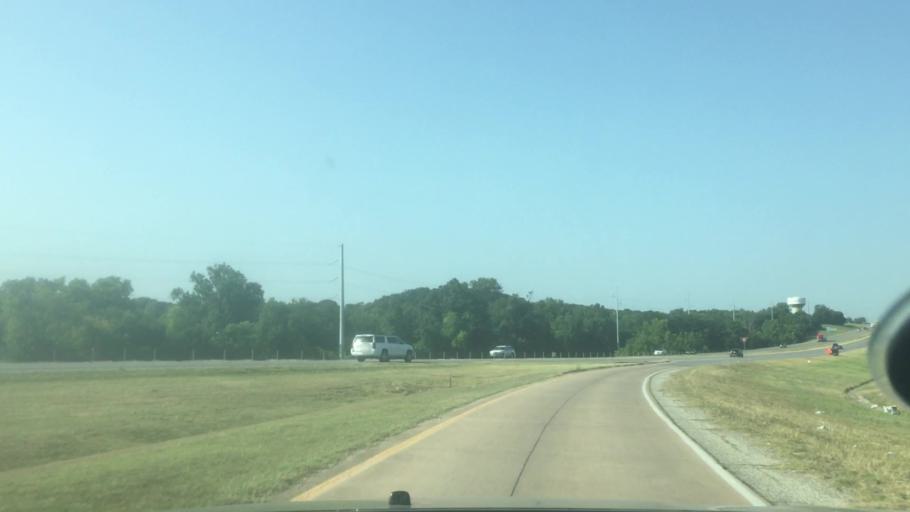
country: US
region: Oklahoma
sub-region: Bryan County
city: Durant
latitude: 34.0190
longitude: -96.3910
